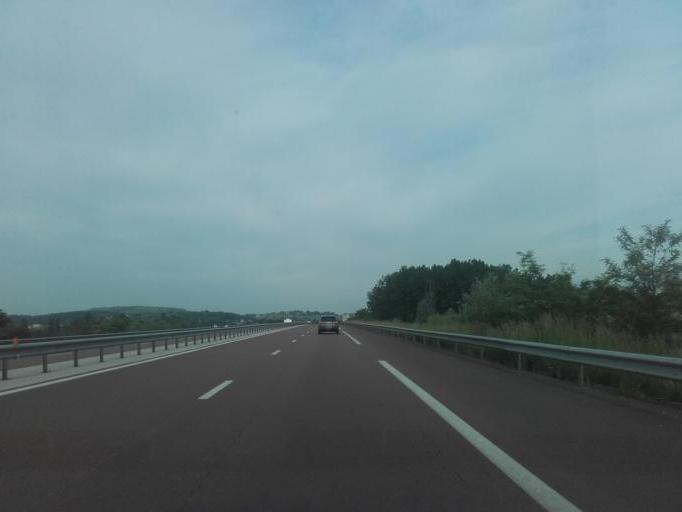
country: FR
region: Bourgogne
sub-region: Departement de Saone-et-Loire
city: Givry
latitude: 46.7594
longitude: 4.7372
